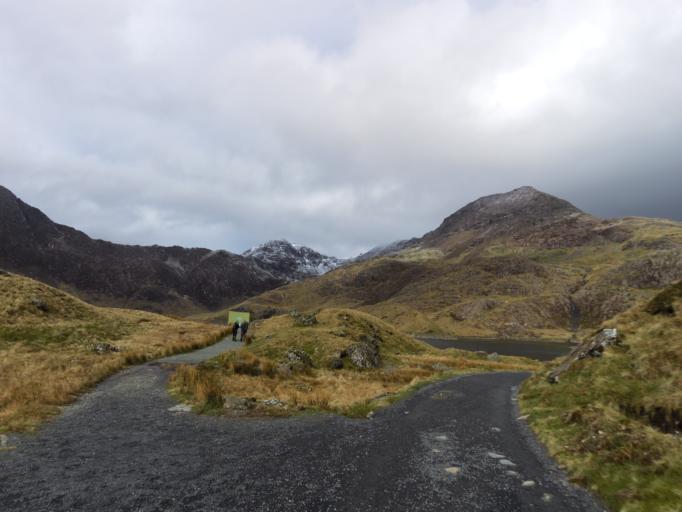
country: GB
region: Wales
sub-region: Gwynedd
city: Llanberis
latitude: 53.0707
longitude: -4.0391
